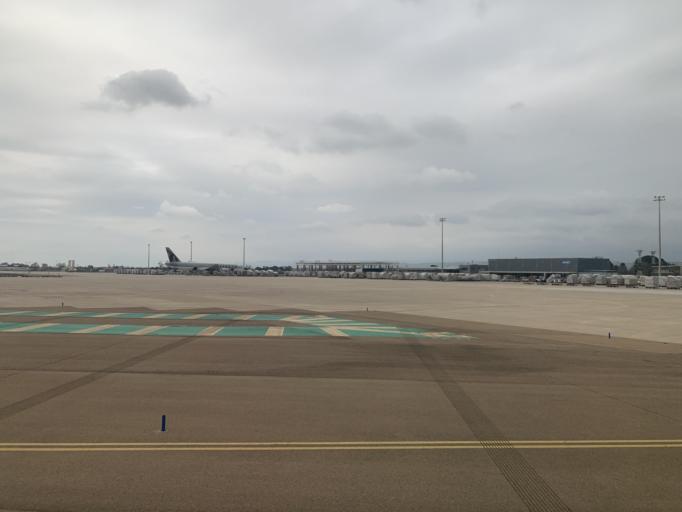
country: ES
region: Aragon
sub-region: Provincia de Zaragoza
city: Utebo
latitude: 41.6621
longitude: -1.0109
